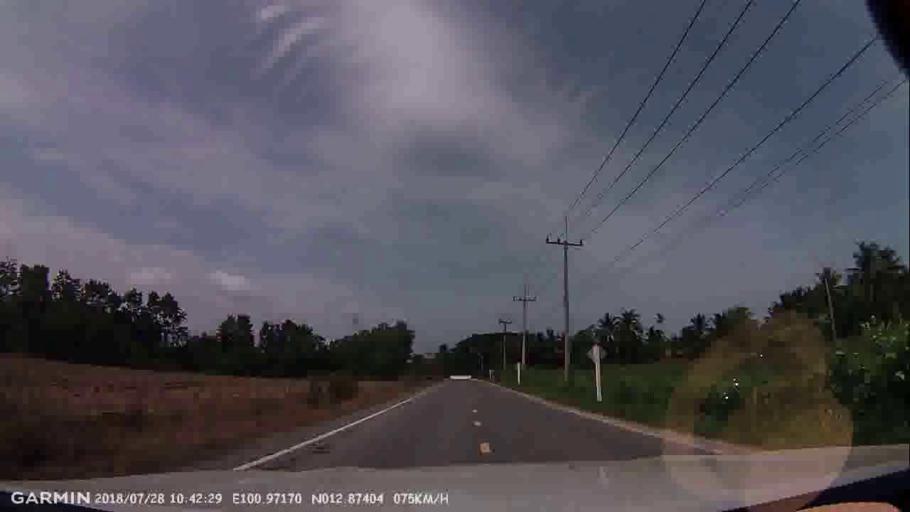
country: TH
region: Chon Buri
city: Phatthaya
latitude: 12.8739
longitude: 100.9716
